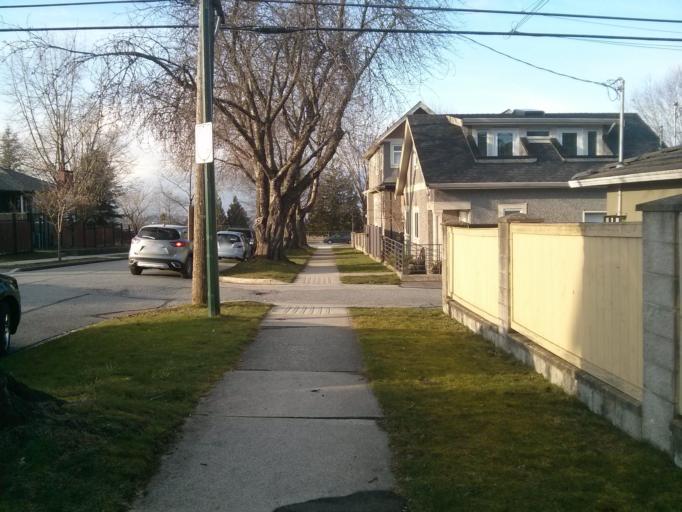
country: CA
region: British Columbia
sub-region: Fraser Valley Regional District
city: North Vancouver
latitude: 49.2498
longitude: -123.0309
